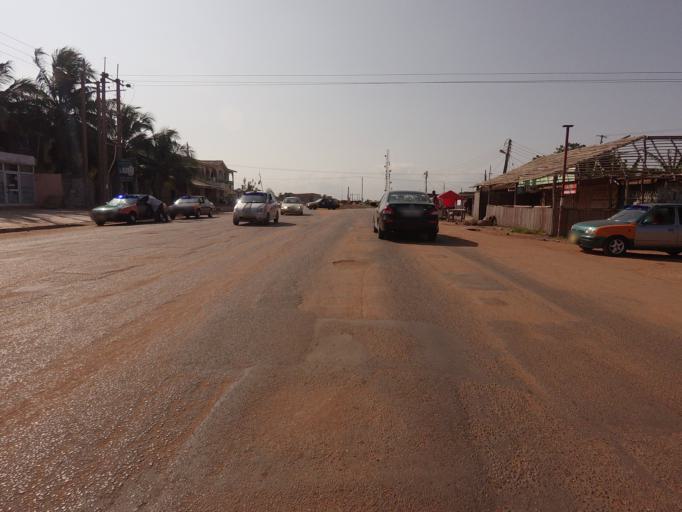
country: GH
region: Greater Accra
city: Teshi Old Town
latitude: 5.6089
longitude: -0.1070
